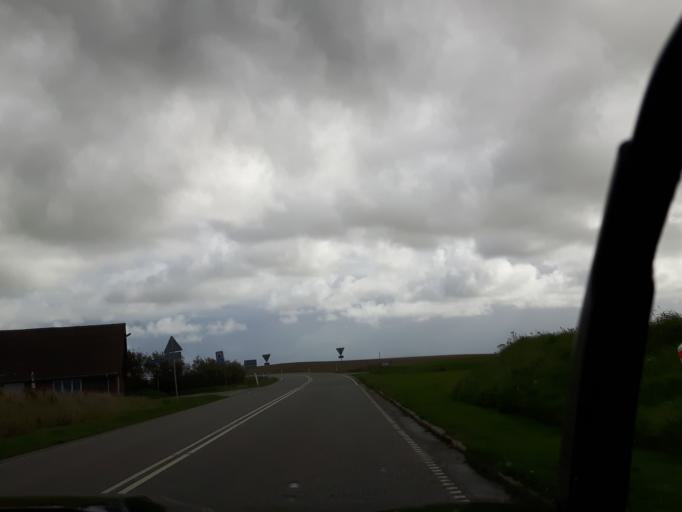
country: DK
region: North Denmark
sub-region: Thisted Kommune
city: Hurup
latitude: 56.7740
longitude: 8.3182
